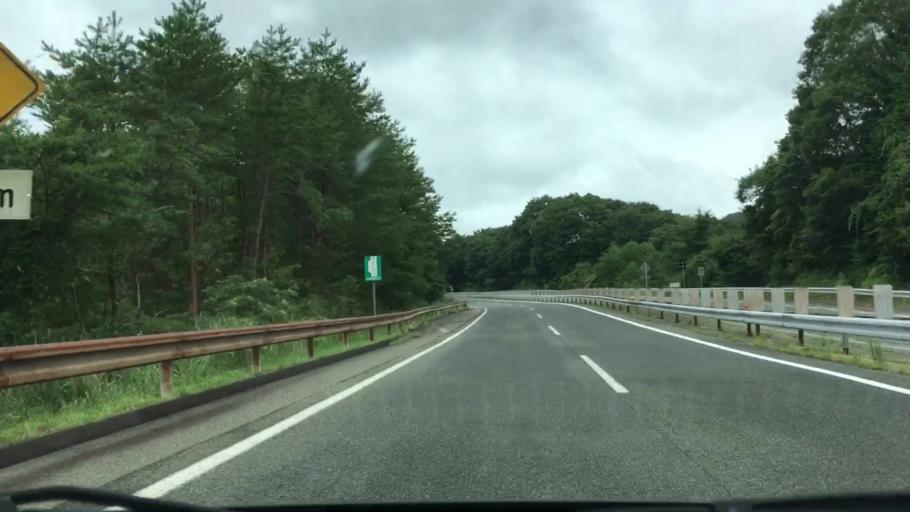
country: JP
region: Hiroshima
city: Shobara
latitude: 34.8718
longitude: 133.1557
